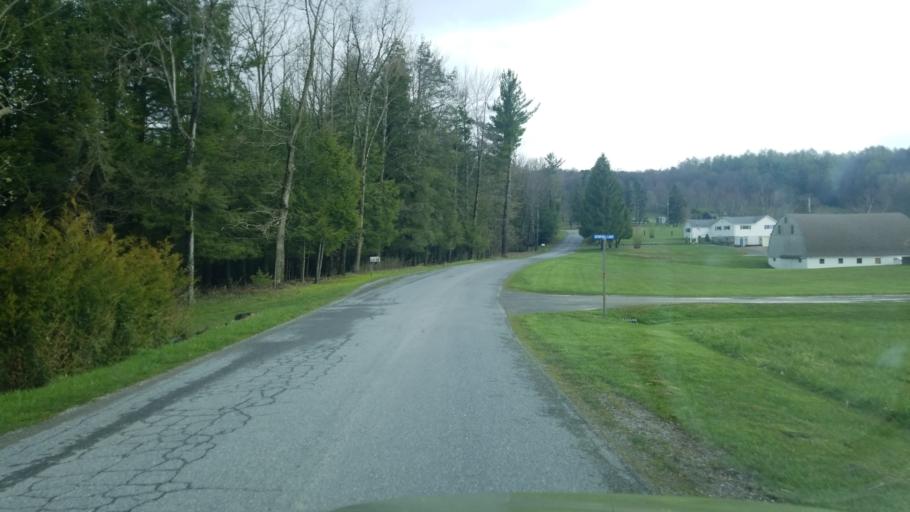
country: US
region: Pennsylvania
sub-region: Clearfield County
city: Shiloh
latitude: 41.1117
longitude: -78.3430
